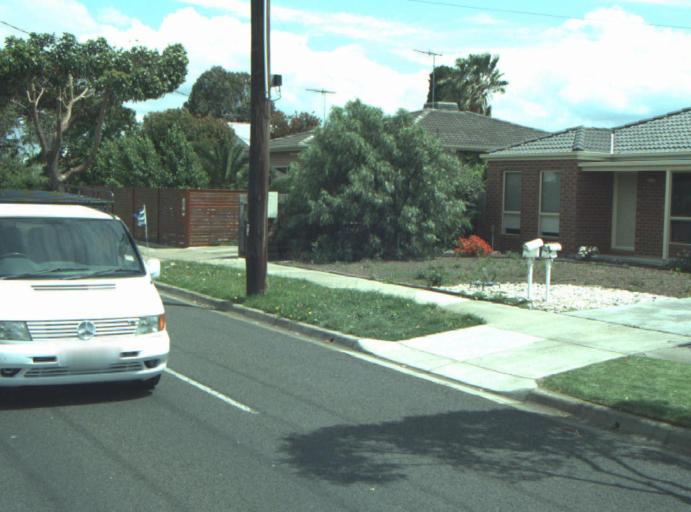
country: AU
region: Victoria
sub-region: Greater Geelong
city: Bell Park
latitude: -38.0881
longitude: 144.3478
